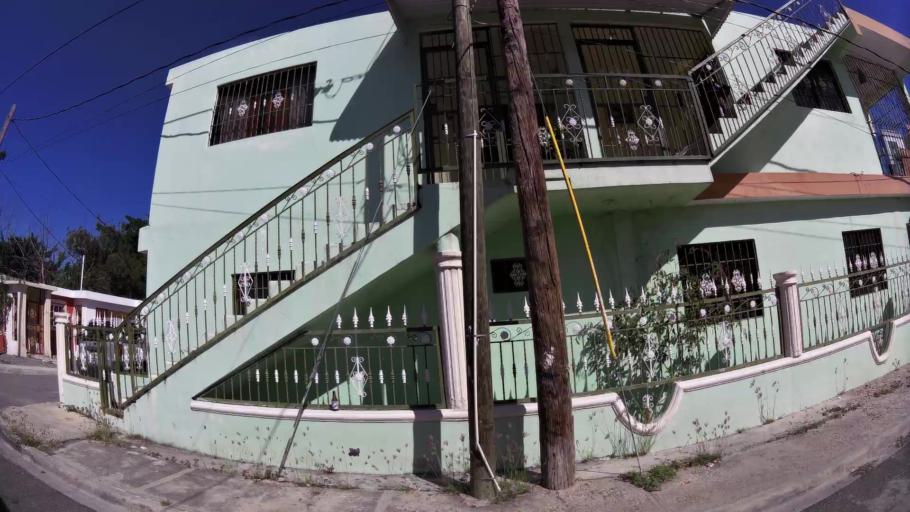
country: DO
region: San Cristobal
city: San Cristobal
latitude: 18.4319
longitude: -70.1228
